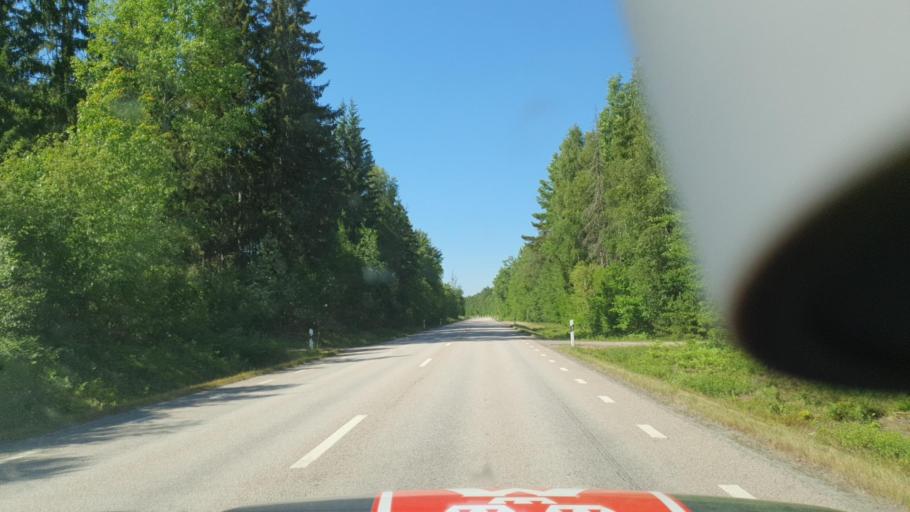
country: SE
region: Kalmar
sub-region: Emmaboda Kommun
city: Emmaboda
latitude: 56.6002
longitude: 15.5668
